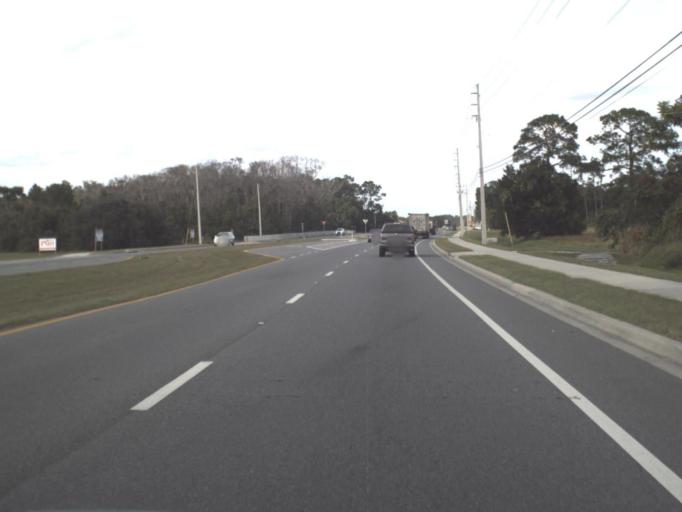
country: US
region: Florida
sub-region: Osceola County
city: Saint Cloud
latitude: 28.3006
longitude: -81.2390
